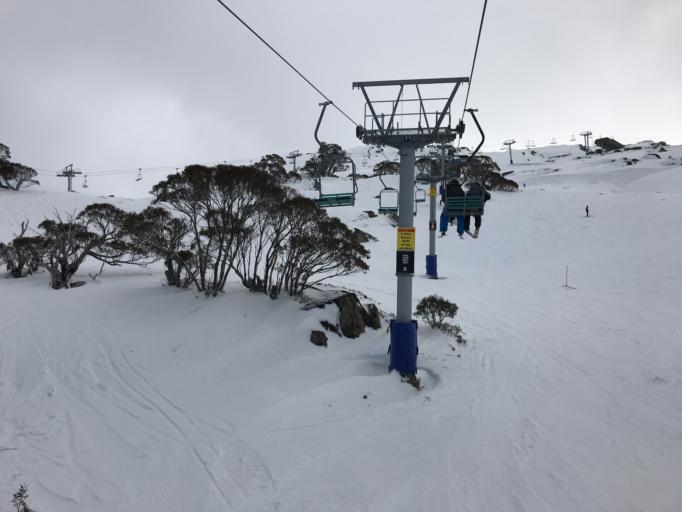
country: AU
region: New South Wales
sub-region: Snowy River
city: Jindabyne
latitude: -36.4005
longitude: 148.3974
